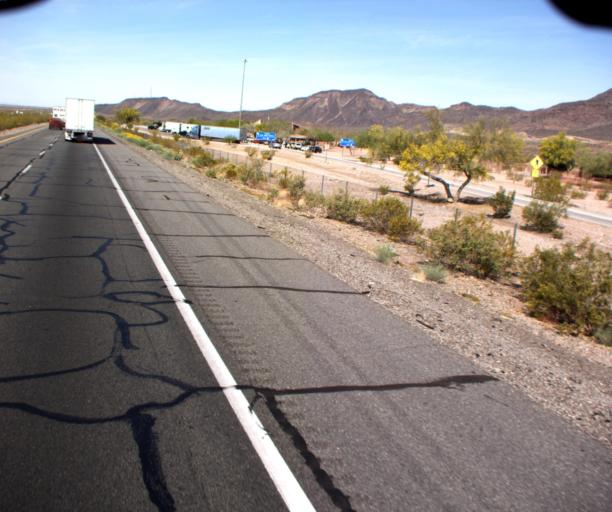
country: US
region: Arizona
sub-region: Maricopa County
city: Buckeye
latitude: 33.5201
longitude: -113.0650
